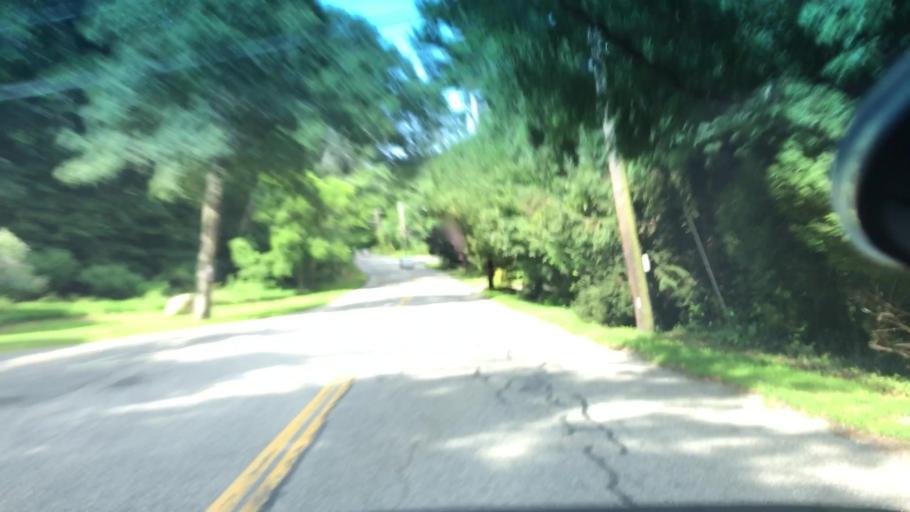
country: US
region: New York
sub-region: Suffolk County
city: Wading River
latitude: 40.9591
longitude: -72.8384
